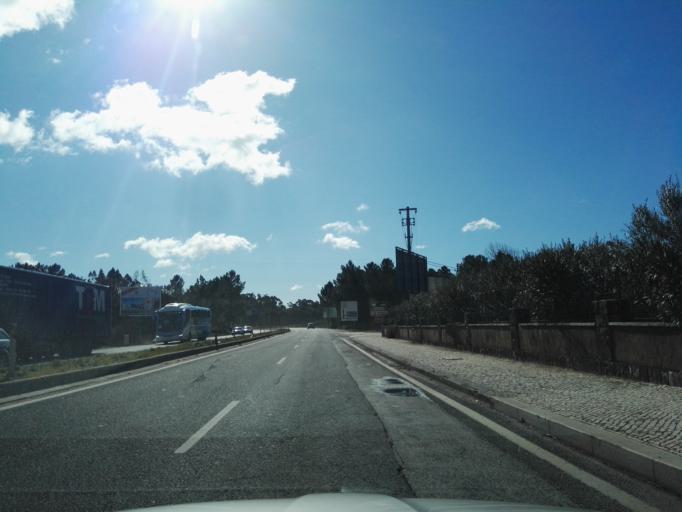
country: PT
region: Santarem
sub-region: Ourem
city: Fatima
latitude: 39.6340
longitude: -8.6841
